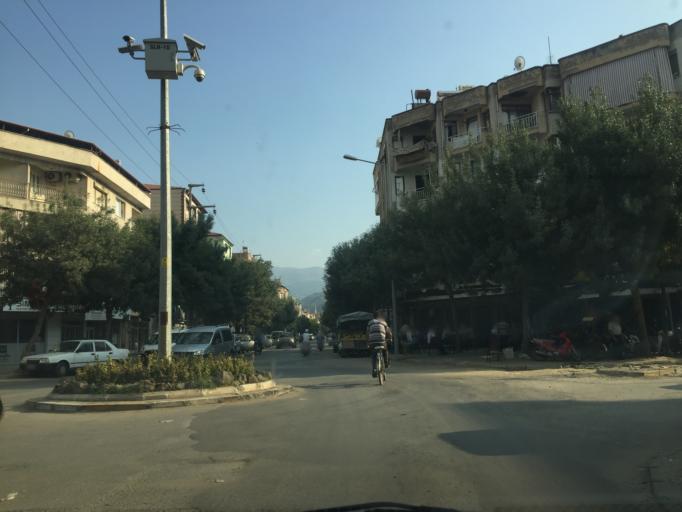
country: TR
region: Manisa
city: Salihli
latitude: 38.4881
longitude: 28.1512
